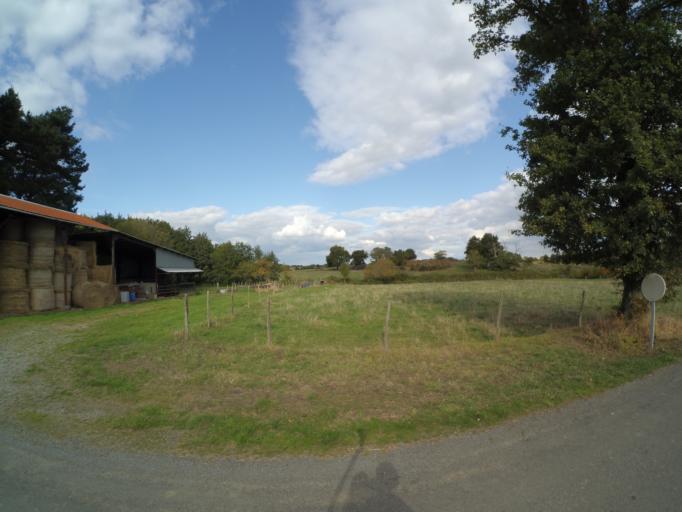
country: FR
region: Pays de la Loire
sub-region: Departement de la Loire-Atlantique
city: Maisdon-sur-Sevre
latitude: 47.0788
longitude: -1.3730
